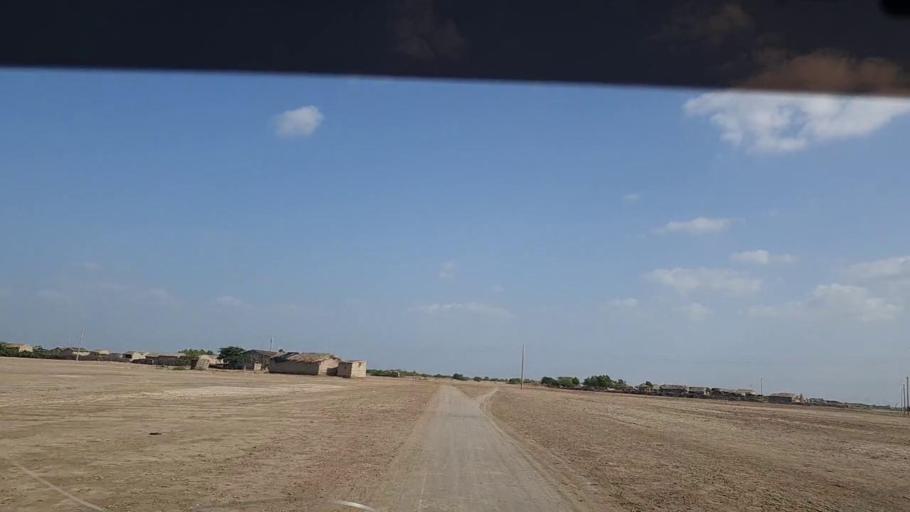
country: PK
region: Sindh
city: Kadhan
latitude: 24.4593
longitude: 68.8559
